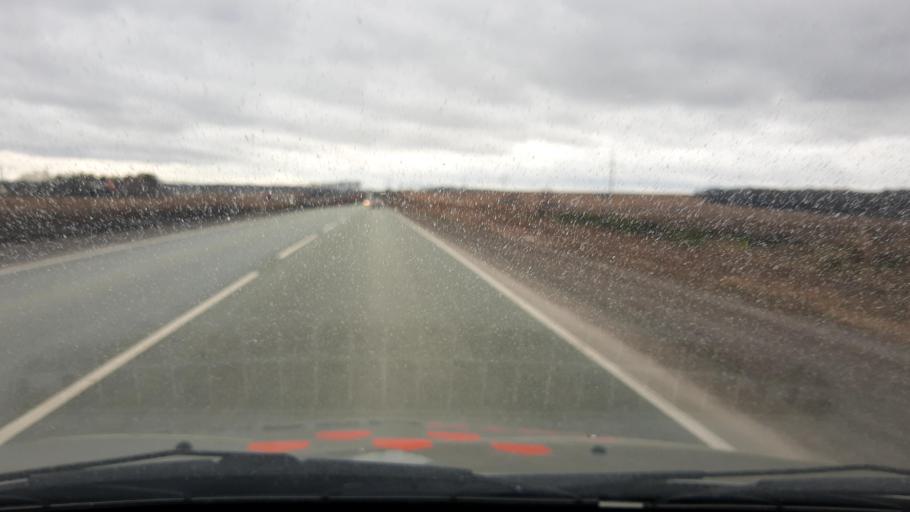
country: RU
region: Bashkortostan
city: Kabakovo
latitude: 54.6966
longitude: 56.2103
